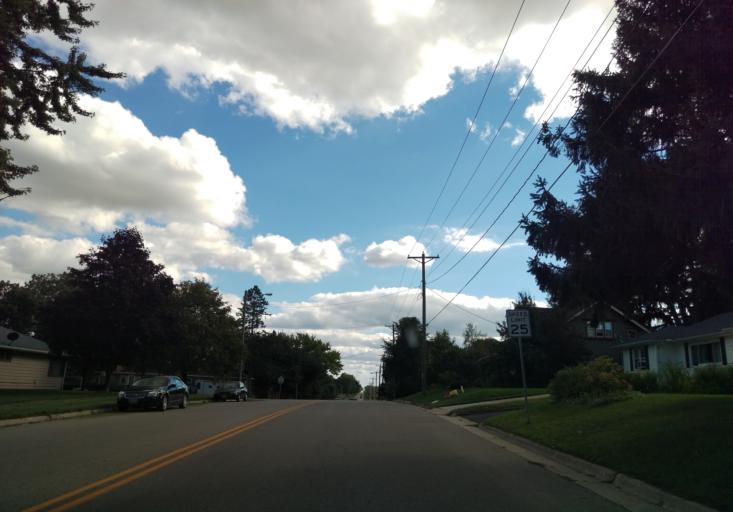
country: US
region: Wisconsin
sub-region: Dane County
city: Stoughton
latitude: 42.9148
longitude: -89.2307
